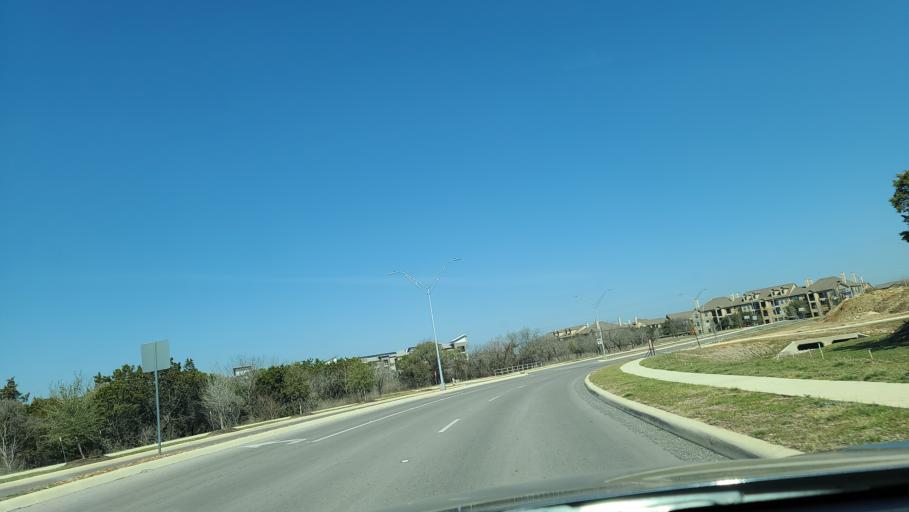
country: US
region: Texas
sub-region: Bexar County
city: Shavano Park
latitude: 29.5737
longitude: -98.6017
